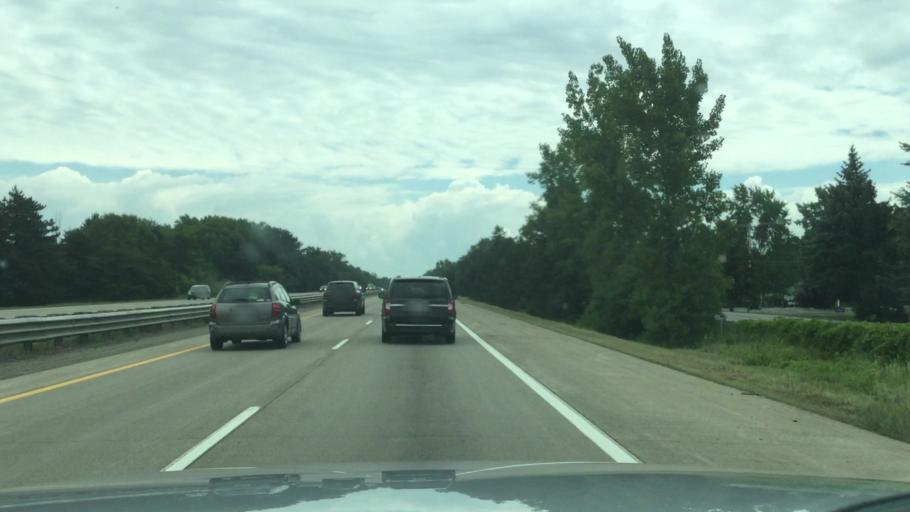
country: US
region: Michigan
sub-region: Genesee County
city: Lake Fenton
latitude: 42.8263
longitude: -83.7304
